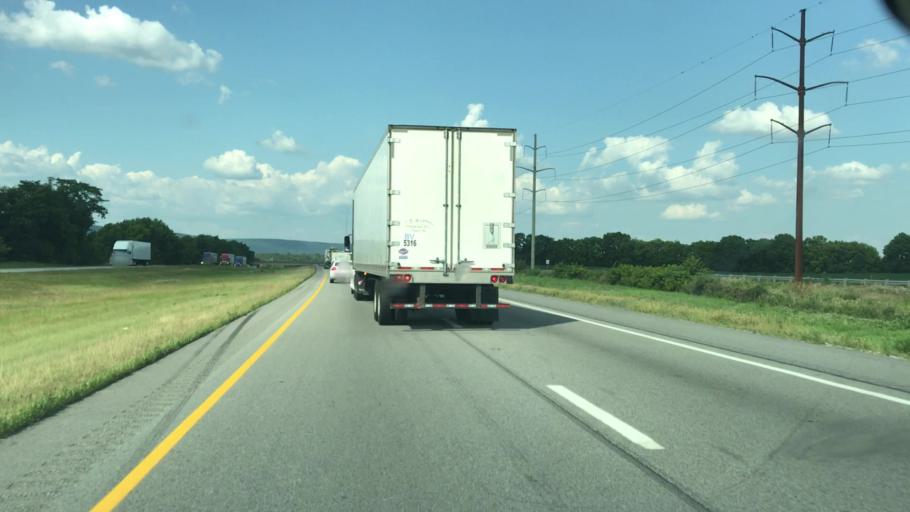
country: US
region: Pennsylvania
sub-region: Cumberland County
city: Mechanicsburg
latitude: 40.2502
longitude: -77.0746
